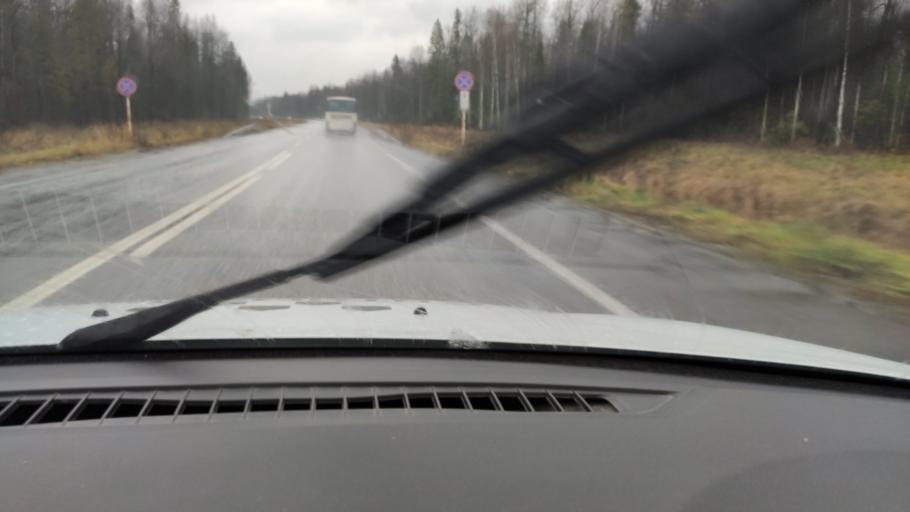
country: RU
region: Perm
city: Novyye Lyady
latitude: 58.0337
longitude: 56.5310
